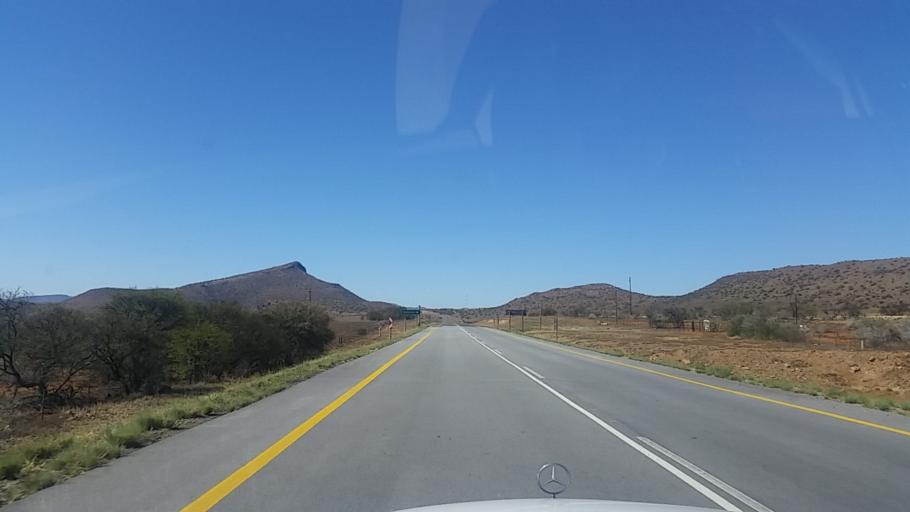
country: ZA
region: Eastern Cape
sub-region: Cacadu District Municipality
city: Graaff-Reinet
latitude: -32.0881
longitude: 24.6030
